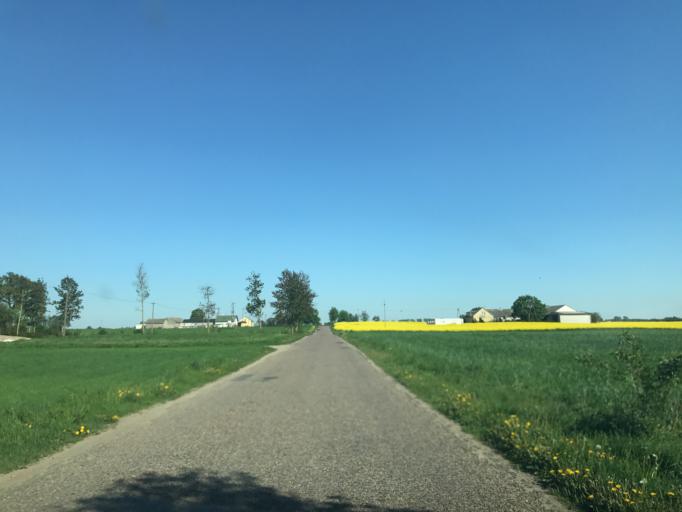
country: PL
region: Kujawsko-Pomorskie
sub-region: Powiat brodnicki
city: Bartniczka
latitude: 53.2074
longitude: 19.5851
